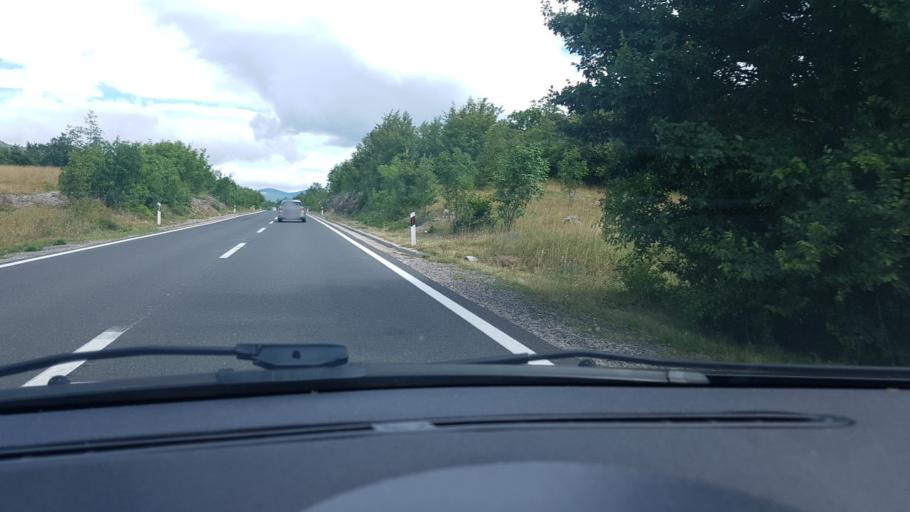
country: HR
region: Zadarska
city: Gracac
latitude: 44.4595
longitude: 15.8133
